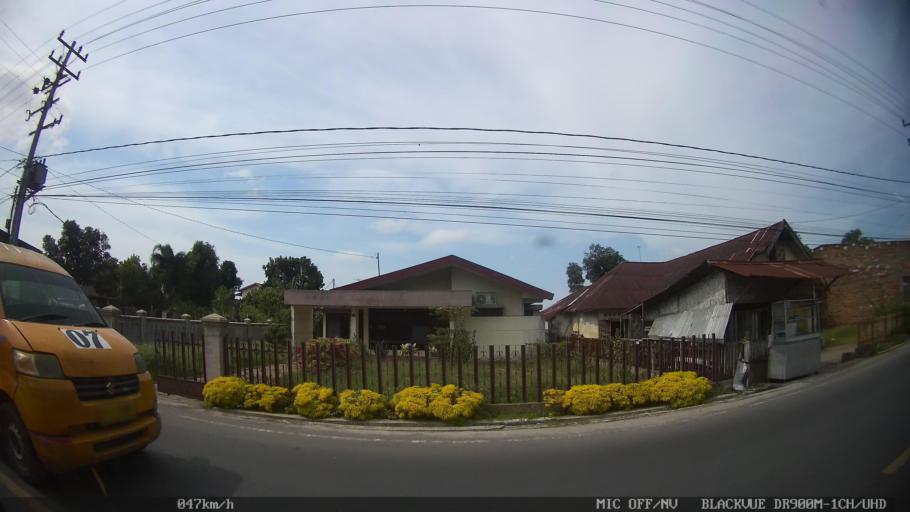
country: ID
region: North Sumatra
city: Percut
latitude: 3.6079
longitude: 98.7755
